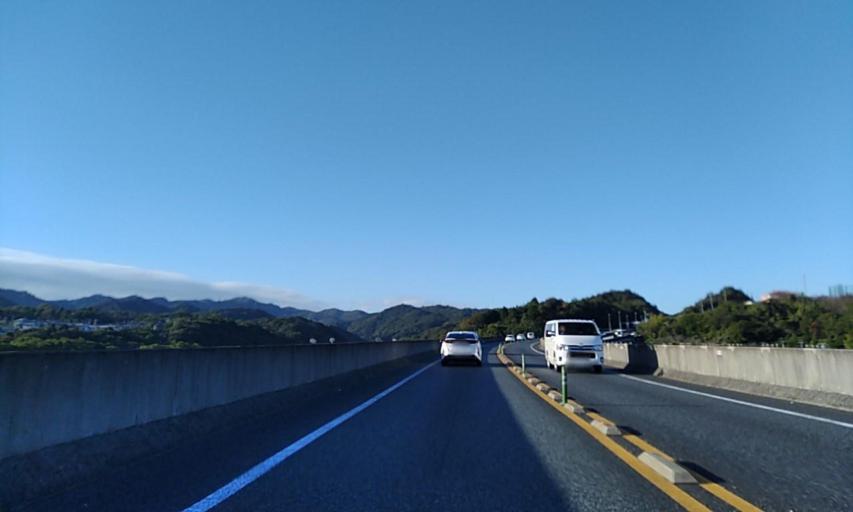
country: JP
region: Wakayama
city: Iwade
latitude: 34.3414
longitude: 135.2490
